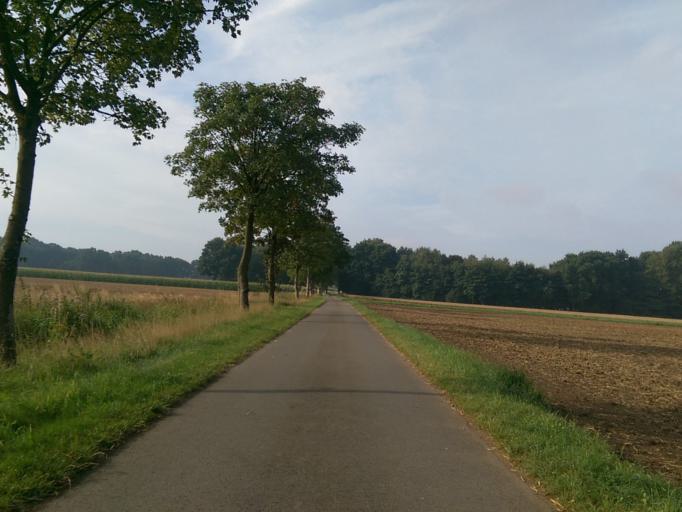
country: DE
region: North Rhine-Westphalia
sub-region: Regierungsbezirk Detmold
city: Guetersloh
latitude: 51.9441
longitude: 8.3194
